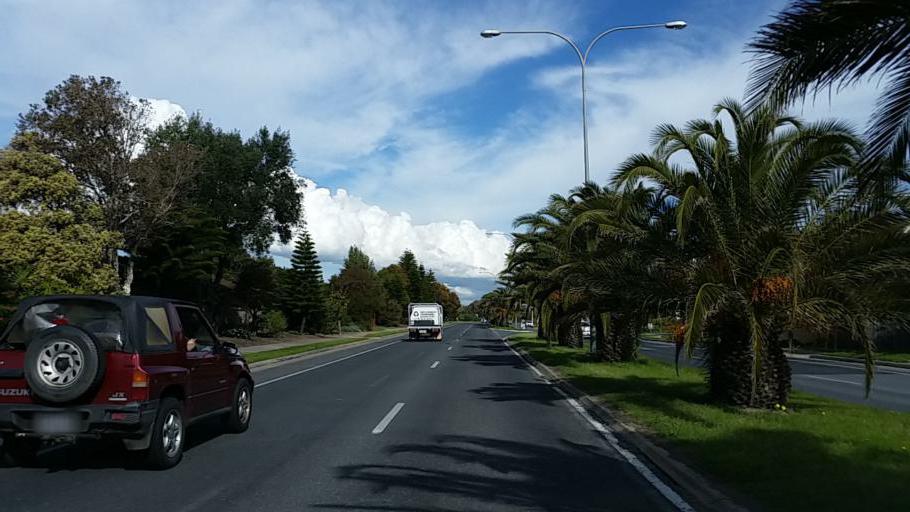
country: AU
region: South Australia
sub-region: Charles Sturt
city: Grange
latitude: -34.8907
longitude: 138.4876
